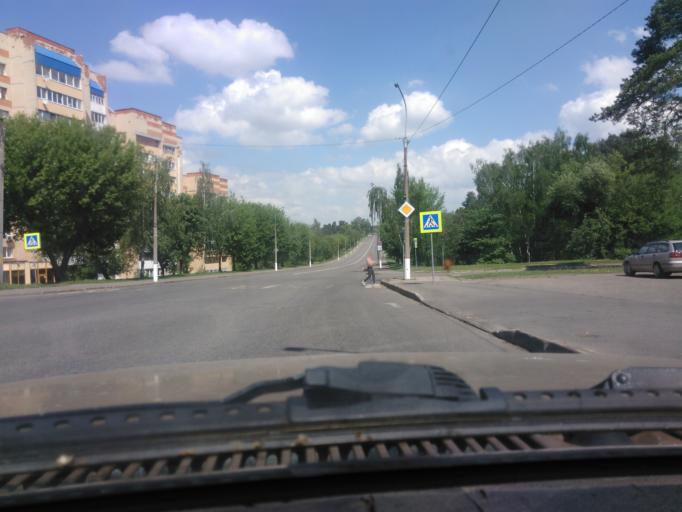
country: BY
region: Mogilev
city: Mahilyow
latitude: 53.9206
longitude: 30.3116
